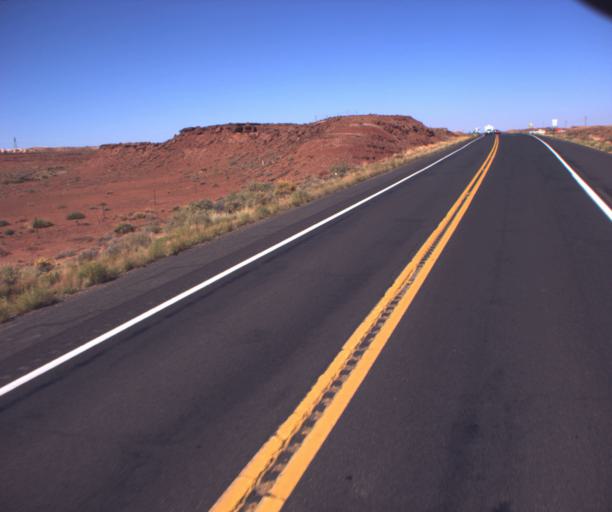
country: US
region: Arizona
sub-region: Coconino County
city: Tuba City
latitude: 35.7916
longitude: -111.4494
